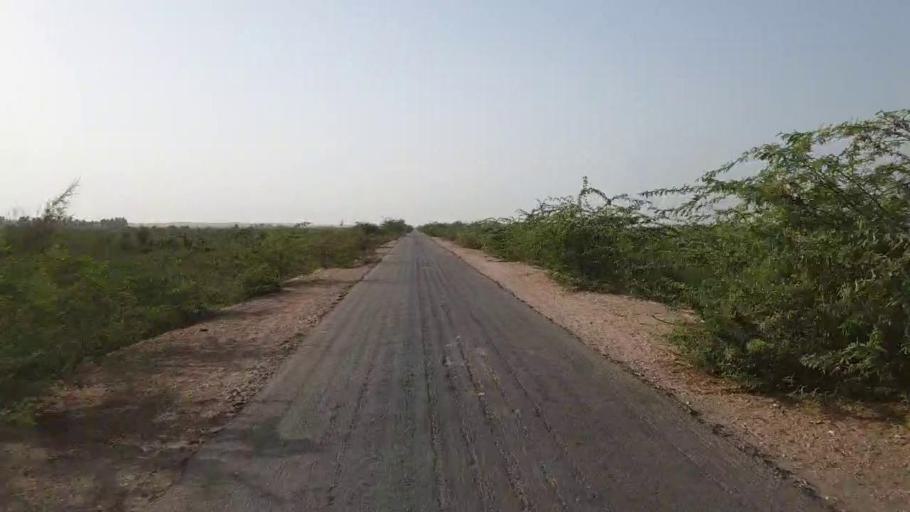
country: PK
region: Sindh
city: Jam Sahib
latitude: 26.4398
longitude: 68.8668
